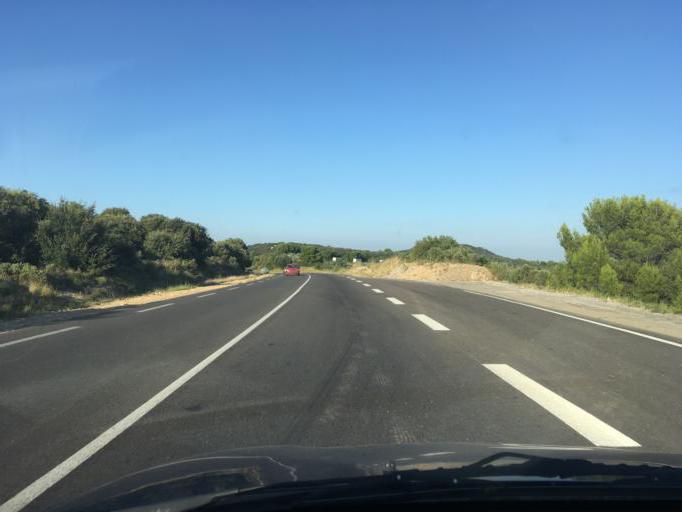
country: FR
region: Languedoc-Roussillon
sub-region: Departement du Gard
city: Ledenon
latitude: 43.8963
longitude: 4.5142
